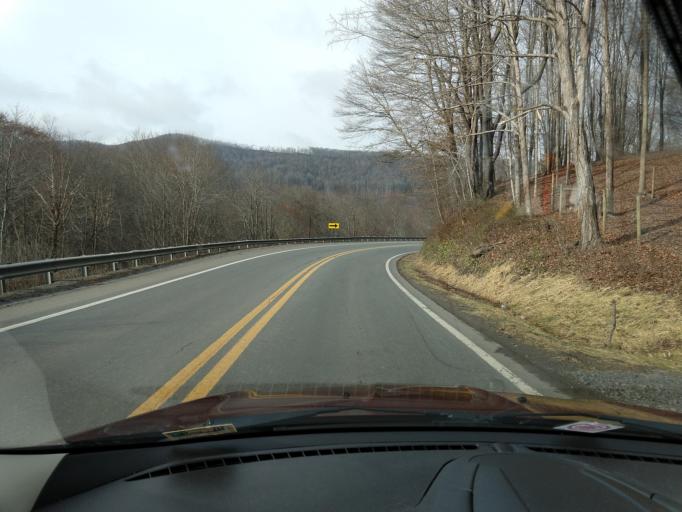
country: US
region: West Virginia
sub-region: Greenbrier County
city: Rainelle
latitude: 37.9689
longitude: -80.7031
